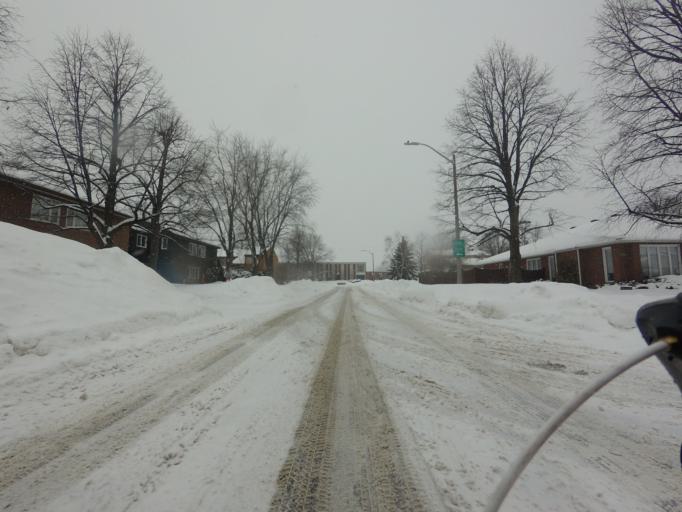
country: CA
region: Ontario
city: Ottawa
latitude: 45.3636
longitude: -75.6836
